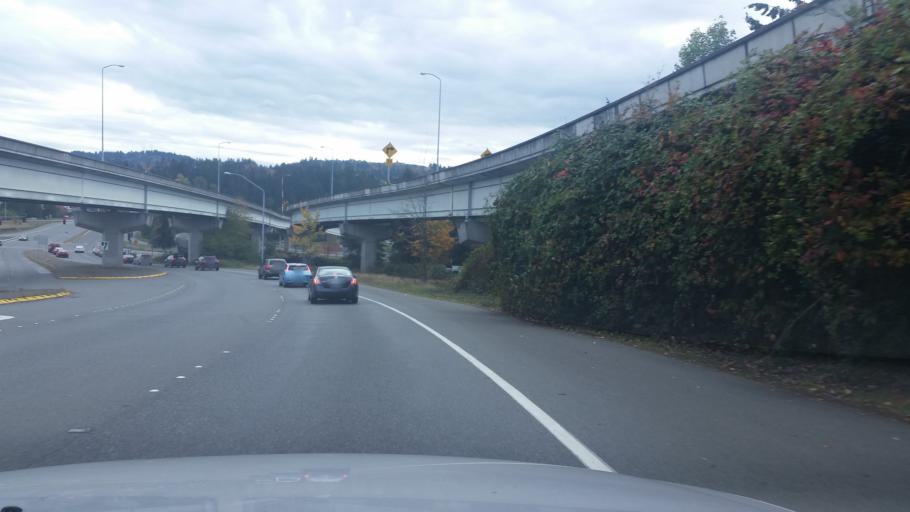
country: US
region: Washington
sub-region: King County
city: Eastgate
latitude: 47.5822
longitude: -122.1429
